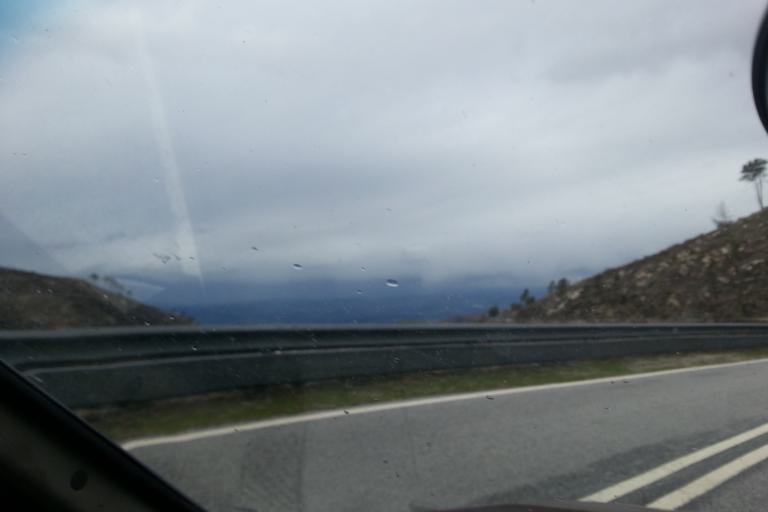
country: PT
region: Guarda
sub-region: Manteigas
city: Manteigas
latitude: 40.4526
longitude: -7.5858
